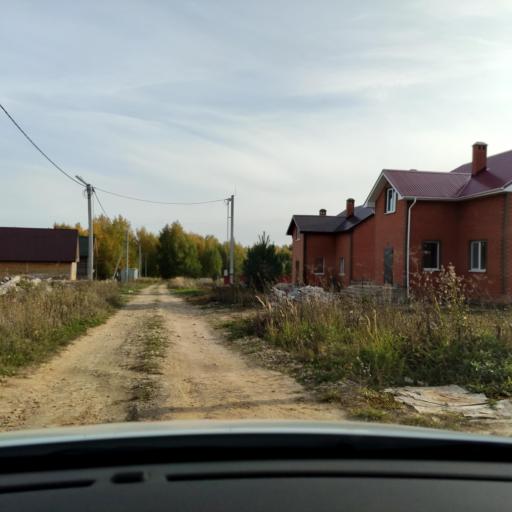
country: RU
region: Tatarstan
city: Vysokaya Gora
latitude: 55.9659
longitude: 49.2088
